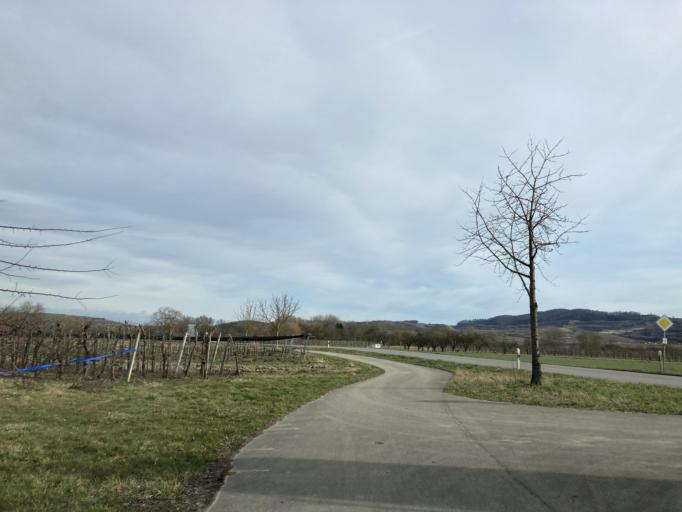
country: DE
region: Baden-Wuerttemberg
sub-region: Freiburg Region
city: Vogtsburg
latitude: 48.0854
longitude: 7.6014
